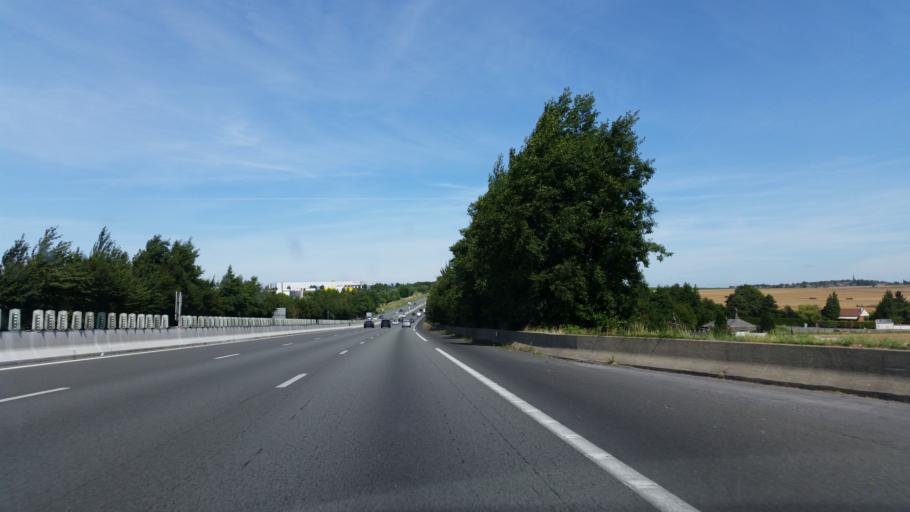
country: FR
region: Nord-Pas-de-Calais
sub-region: Departement du Pas-de-Calais
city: Feuchy
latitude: 50.2478
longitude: 2.8564
